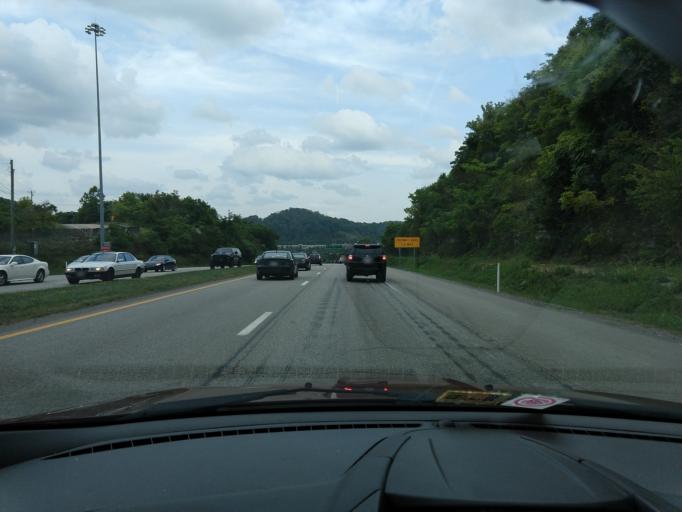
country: US
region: West Virginia
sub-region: Harrison County
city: Despard
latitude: 39.2777
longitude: -80.2924
